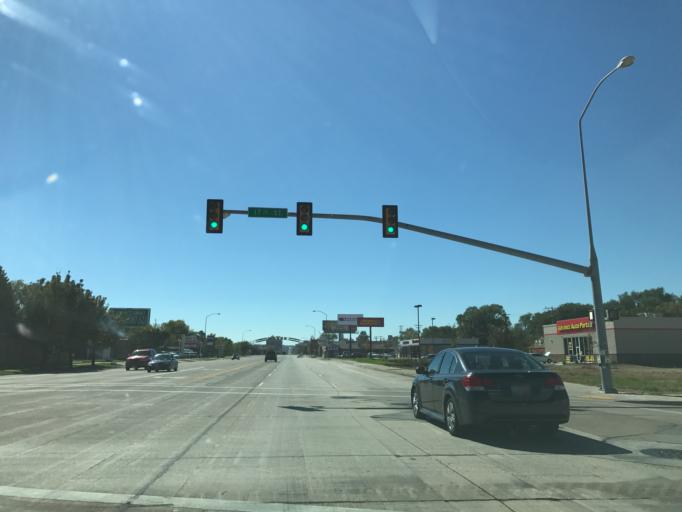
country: US
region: Utah
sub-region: Weber County
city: Ogden
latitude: 41.2369
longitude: -111.9702
